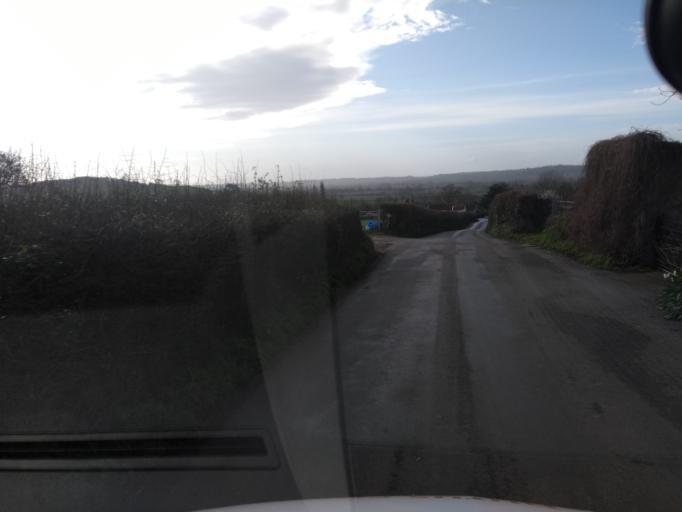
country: GB
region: England
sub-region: Somerset
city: Street
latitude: 51.1294
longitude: -2.8245
